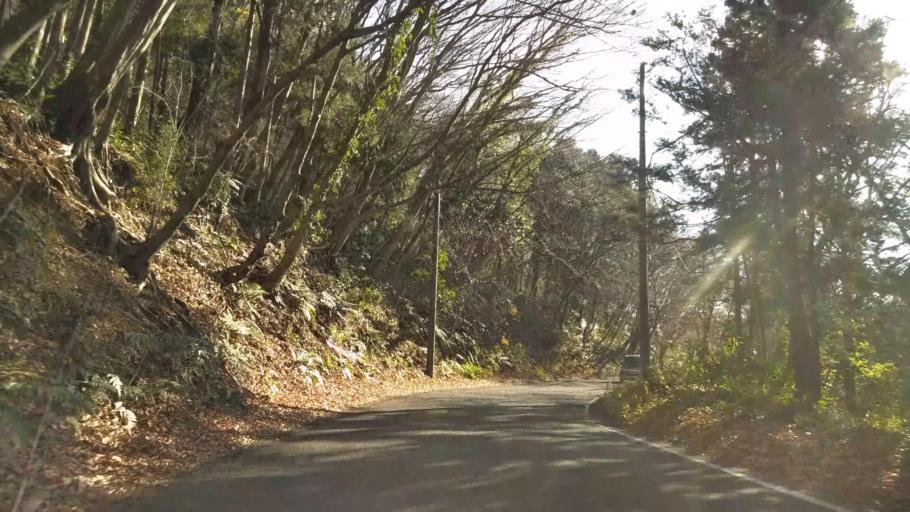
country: JP
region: Kanagawa
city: Hadano
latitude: 35.3735
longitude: 139.2413
